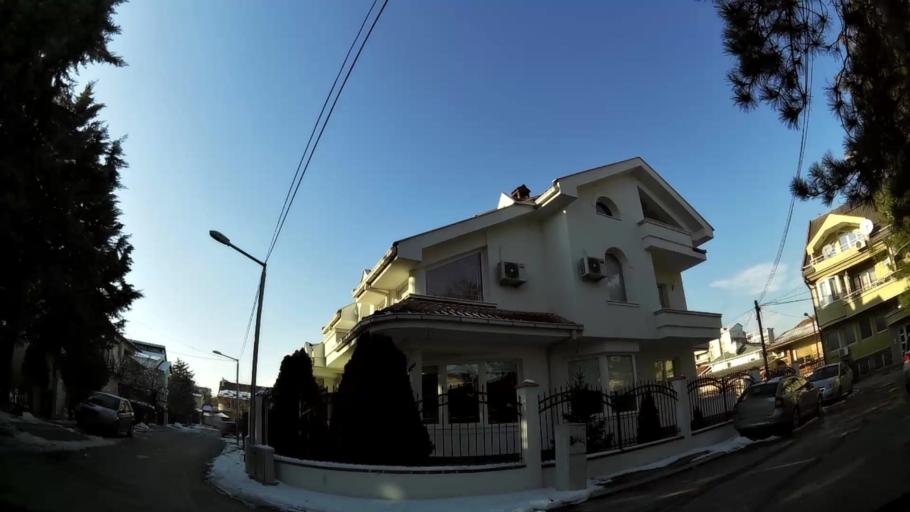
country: MK
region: Karpos
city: Skopje
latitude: 42.0019
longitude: 21.3939
